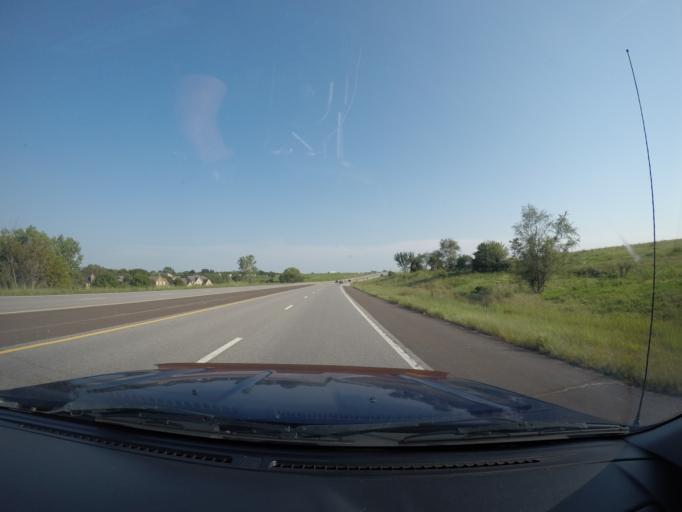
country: US
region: Kansas
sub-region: Wyandotte County
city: Bonner Springs
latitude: 39.0401
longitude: -94.8552
